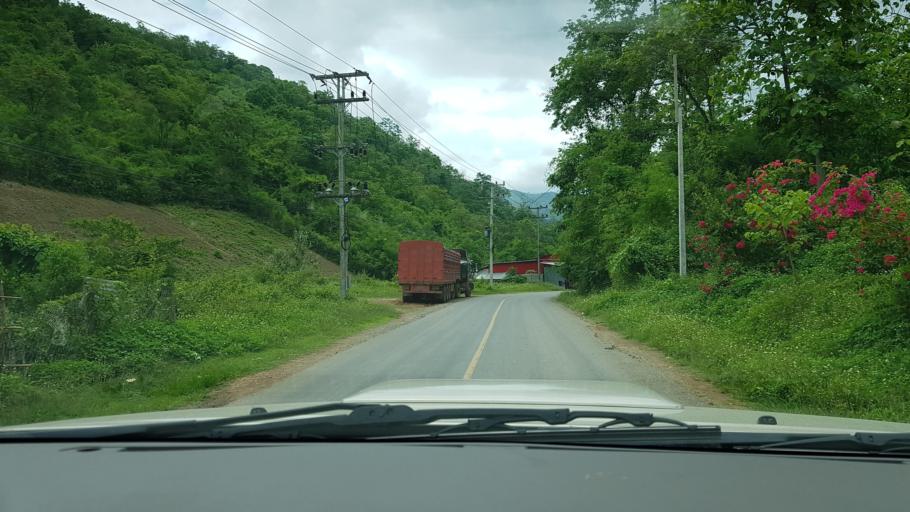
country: TH
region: Nan
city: Chaloem Phra Kiat
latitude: 19.9710
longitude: 101.2673
